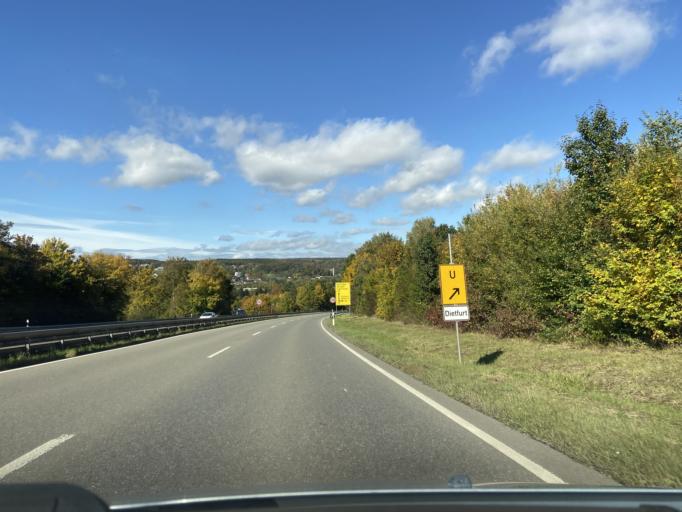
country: DE
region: Baden-Wuerttemberg
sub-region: Tuebingen Region
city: Sigmaringen
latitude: 48.0742
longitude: 9.2085
